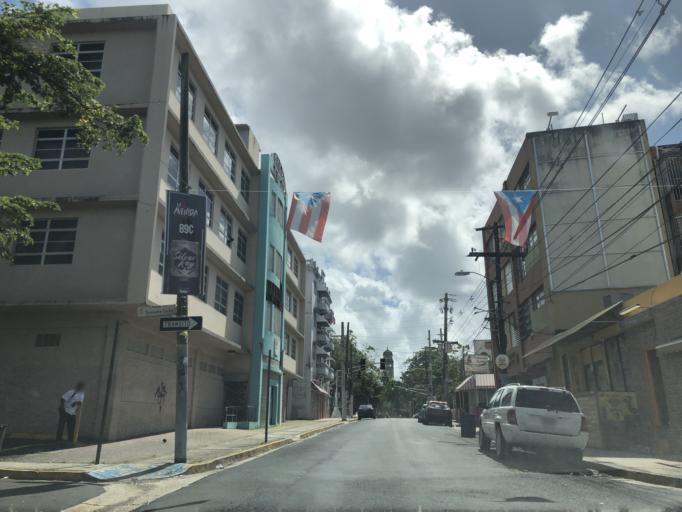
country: PR
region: Trujillo Alto
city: Trujillo Alto
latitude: 18.4031
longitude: -66.0544
